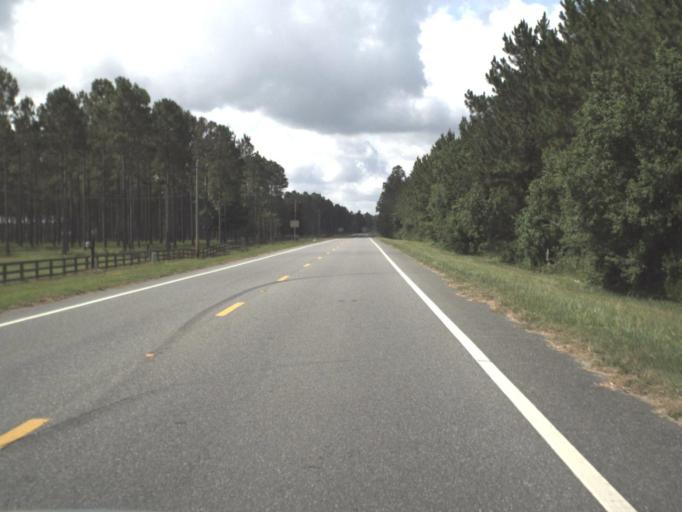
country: US
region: Florida
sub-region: Baker County
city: Macclenny
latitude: 30.3214
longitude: -82.1250
